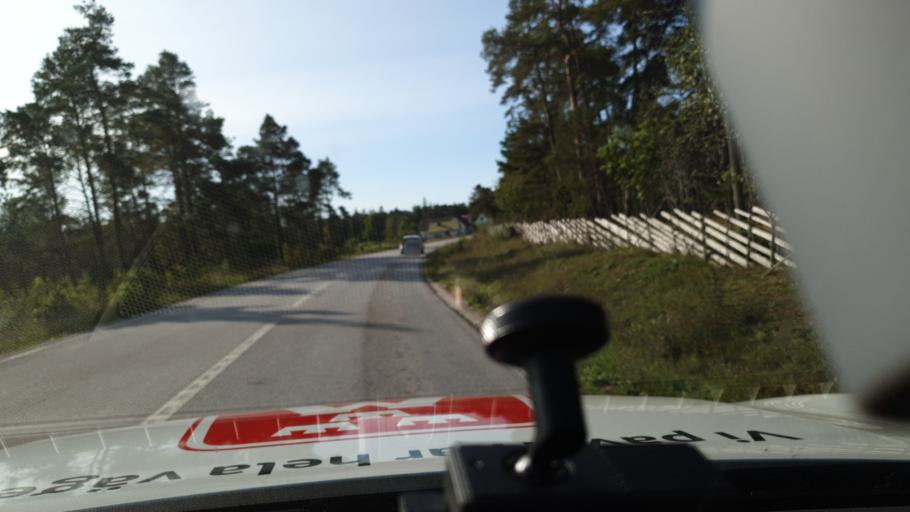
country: SE
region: Gotland
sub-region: Gotland
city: Klintehamn
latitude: 57.3268
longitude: 18.1932
